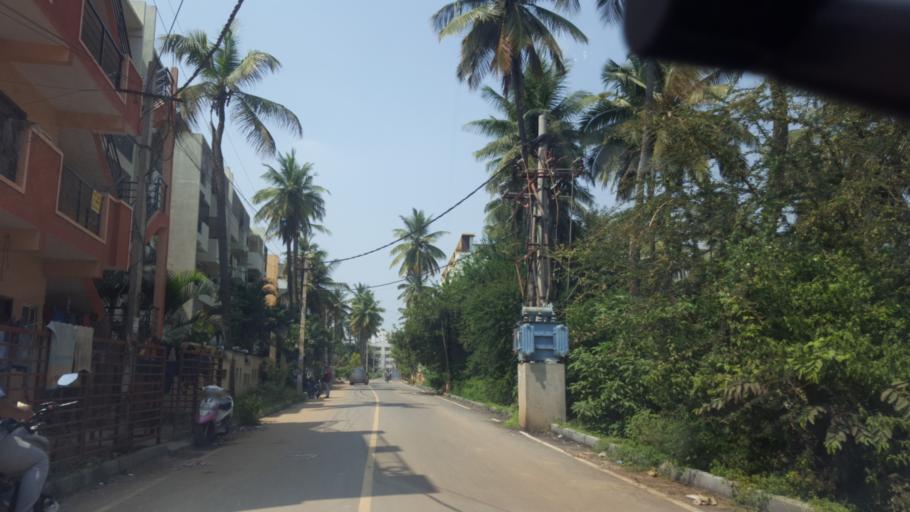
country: IN
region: Karnataka
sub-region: Bangalore Urban
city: Bangalore
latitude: 12.9403
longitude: 77.7053
